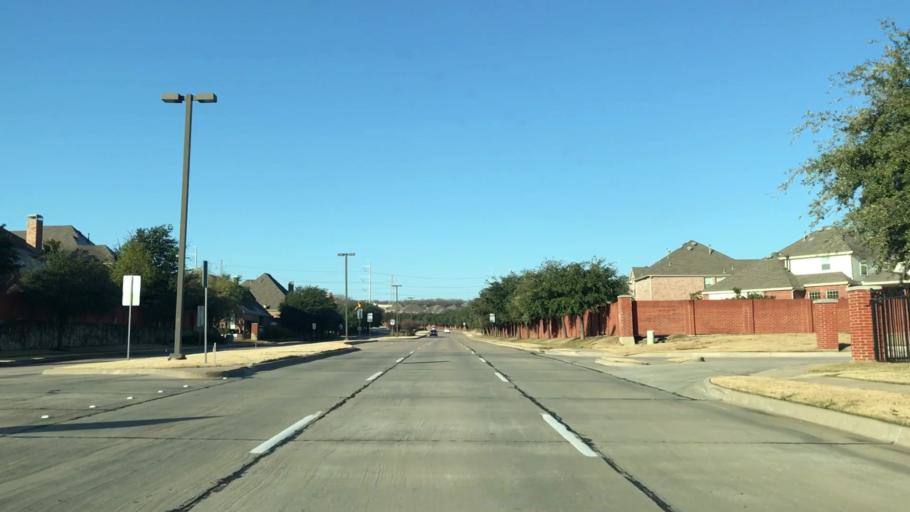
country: US
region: Texas
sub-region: Dallas County
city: Coppell
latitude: 32.9273
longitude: -96.9591
